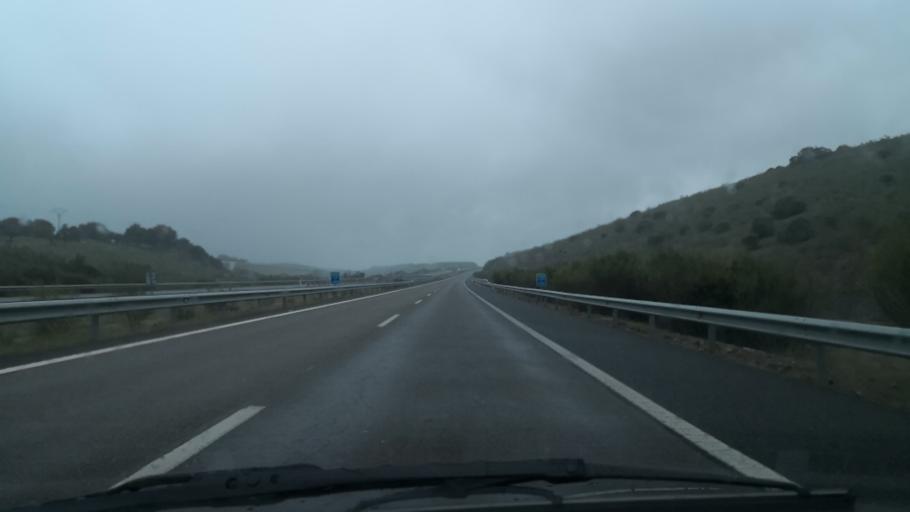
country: ES
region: Extremadura
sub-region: Provincia de Caceres
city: Casas de Millan
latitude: 39.8583
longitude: -6.3152
